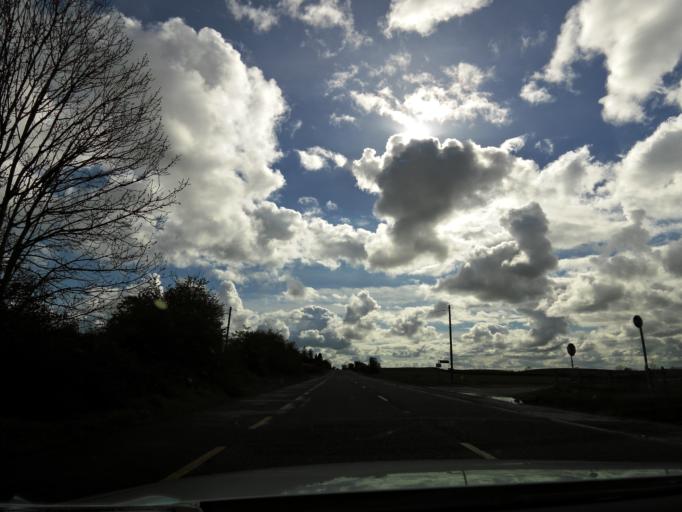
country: IE
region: Leinster
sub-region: Laois
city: Rathdowney
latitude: 52.8069
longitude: -7.4946
